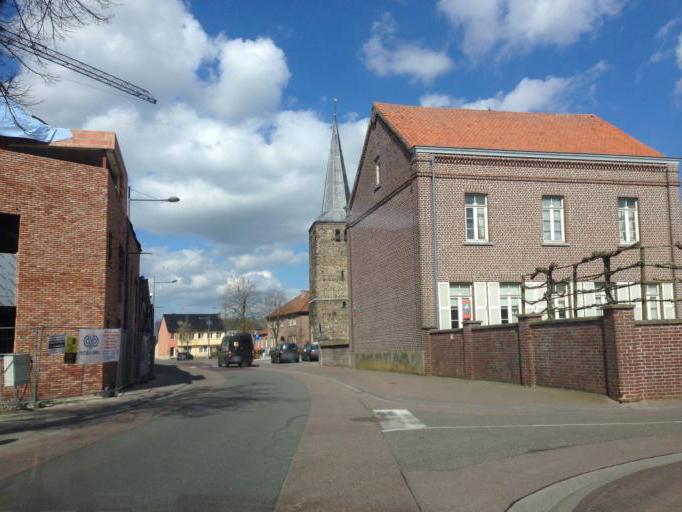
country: BE
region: Flanders
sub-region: Provincie Limburg
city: Bree
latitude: 51.1543
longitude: 5.6029
